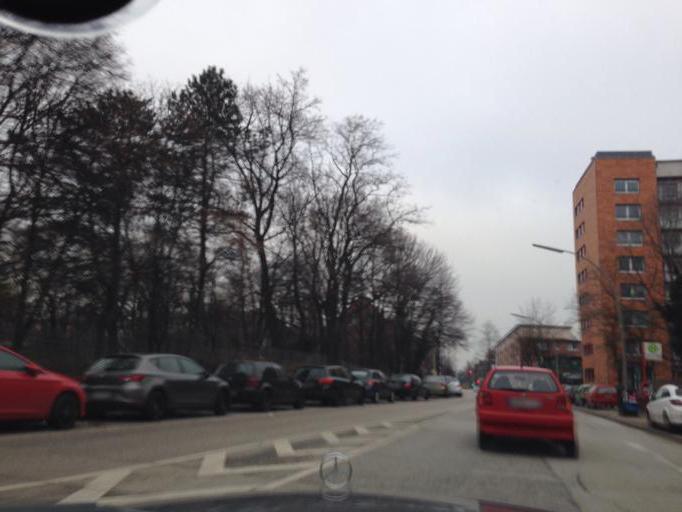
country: DE
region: Hamburg
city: Borgfelde
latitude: 53.5670
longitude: 10.0403
